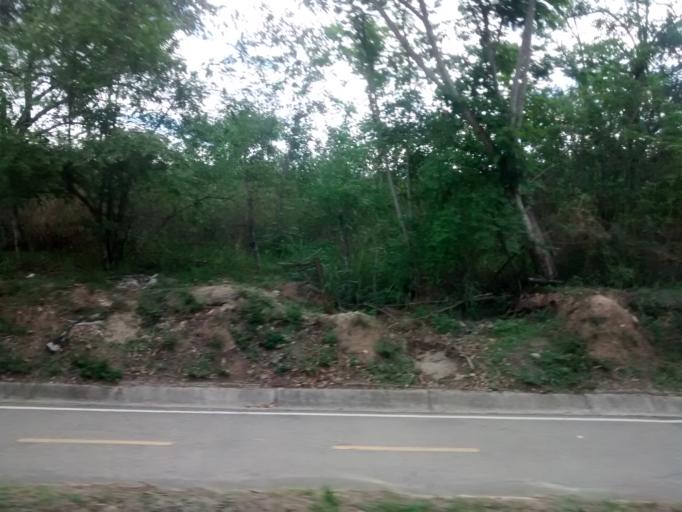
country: CO
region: Cundinamarca
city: Ricaurte
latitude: 4.2740
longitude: -74.7569
